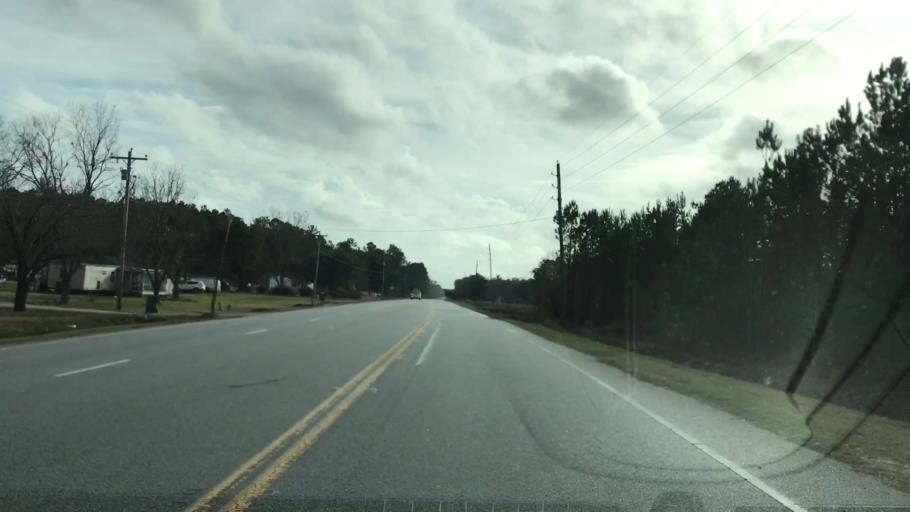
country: US
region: South Carolina
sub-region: Williamsburg County
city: Andrews
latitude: 33.4418
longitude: -79.5912
